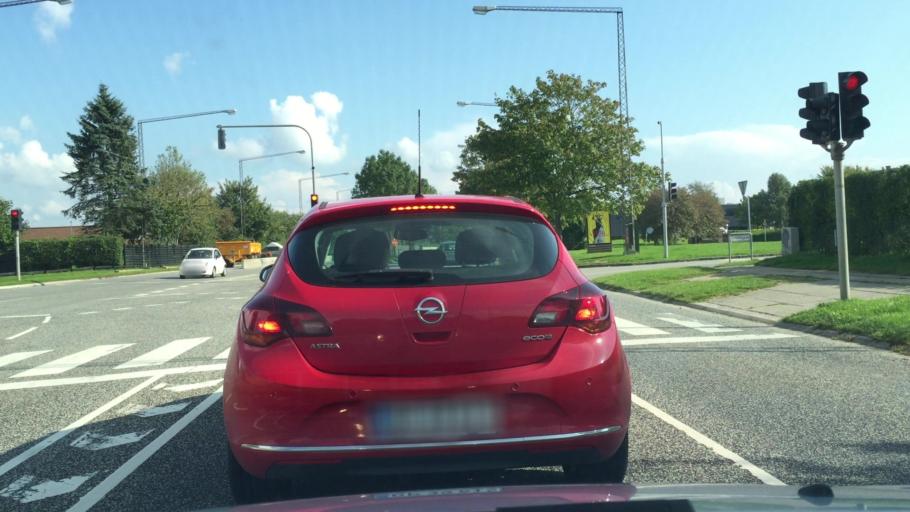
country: DK
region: Central Jutland
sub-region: Arhus Kommune
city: Arhus
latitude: 56.1969
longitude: 10.2148
